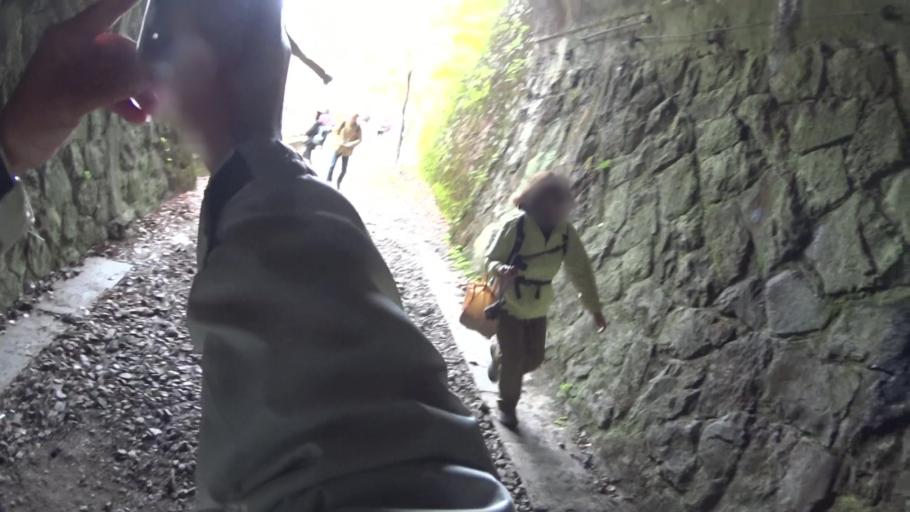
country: JP
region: Hyogo
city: Takarazuka
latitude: 34.8503
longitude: 135.3149
